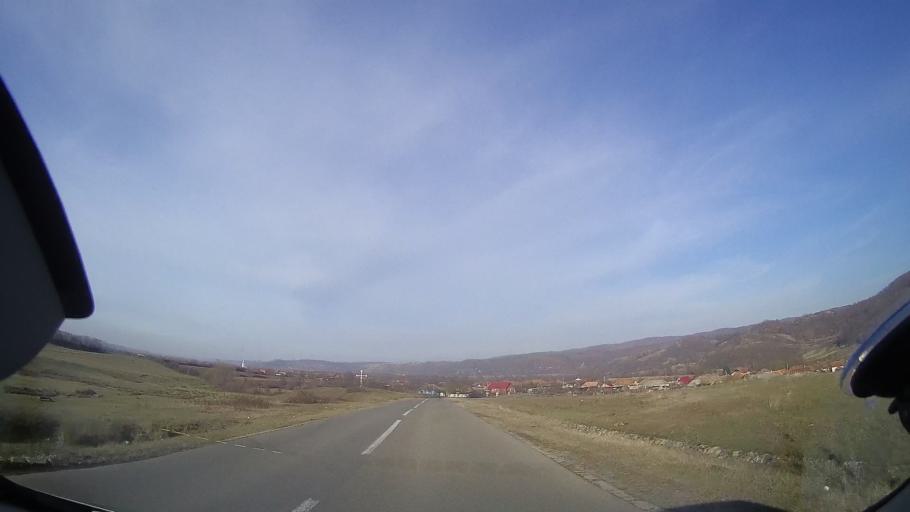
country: RO
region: Bihor
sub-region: Comuna Brusturi
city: Brusturi
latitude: 47.1338
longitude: 22.2685
